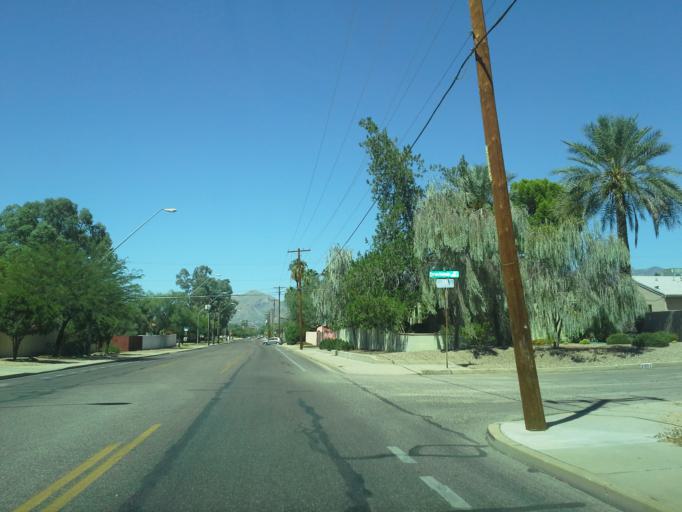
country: US
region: Arizona
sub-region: Pima County
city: Tucson
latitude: 32.2395
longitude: -110.9353
